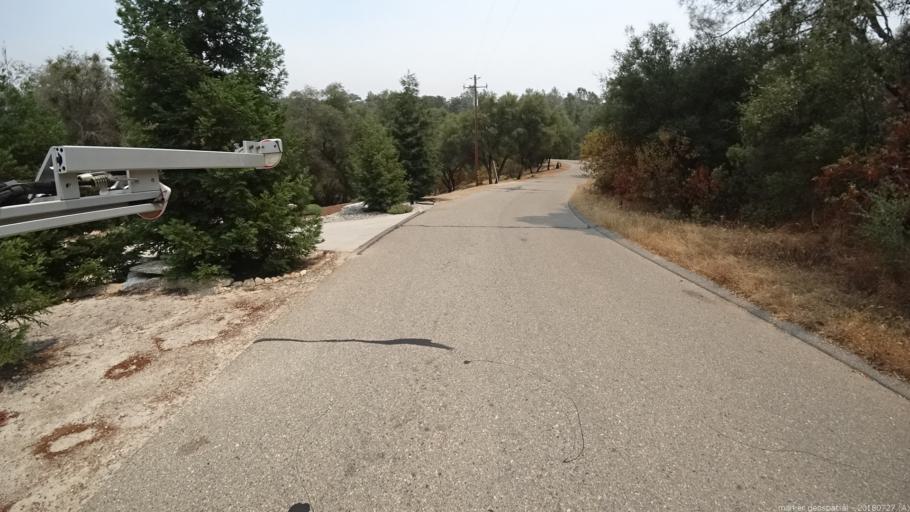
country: US
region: California
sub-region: Madera County
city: Coarsegold
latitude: 37.2492
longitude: -119.7075
